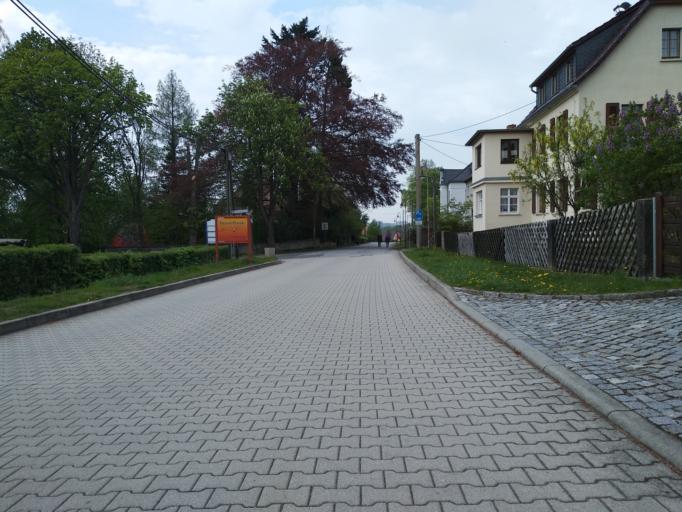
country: DE
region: Saxony
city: Hohnstein
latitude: 50.9758
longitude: 14.1133
